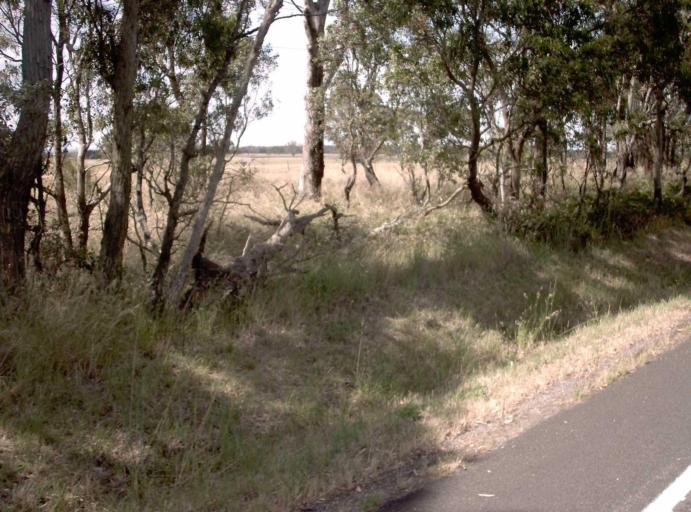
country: AU
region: Victoria
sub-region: Wellington
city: Sale
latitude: -37.9302
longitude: 147.1995
